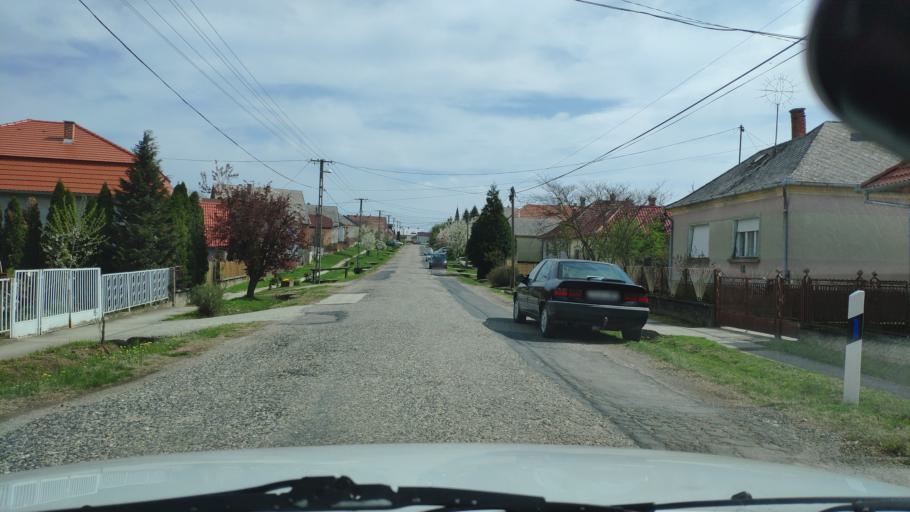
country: HU
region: Zala
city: Nagykanizsa
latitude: 46.4236
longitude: 17.0267
